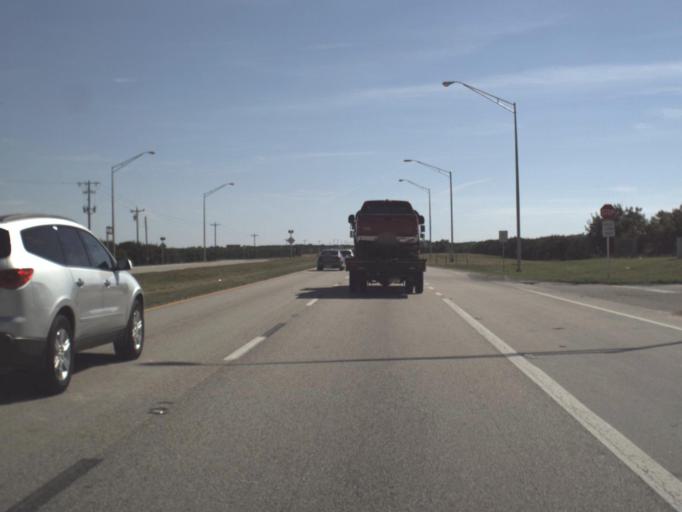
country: US
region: Florida
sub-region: Highlands County
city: Placid Lakes
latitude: 27.2080
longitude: -81.3288
